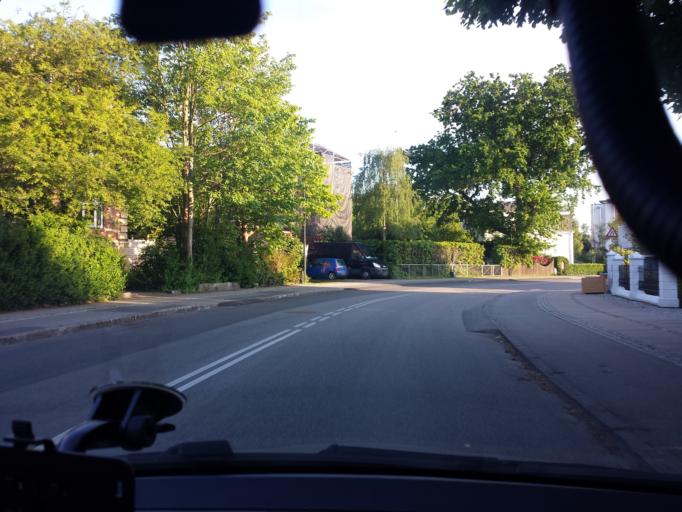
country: DK
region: Capital Region
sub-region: Gentofte Kommune
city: Charlottenlund
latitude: 55.7555
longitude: 12.5753
